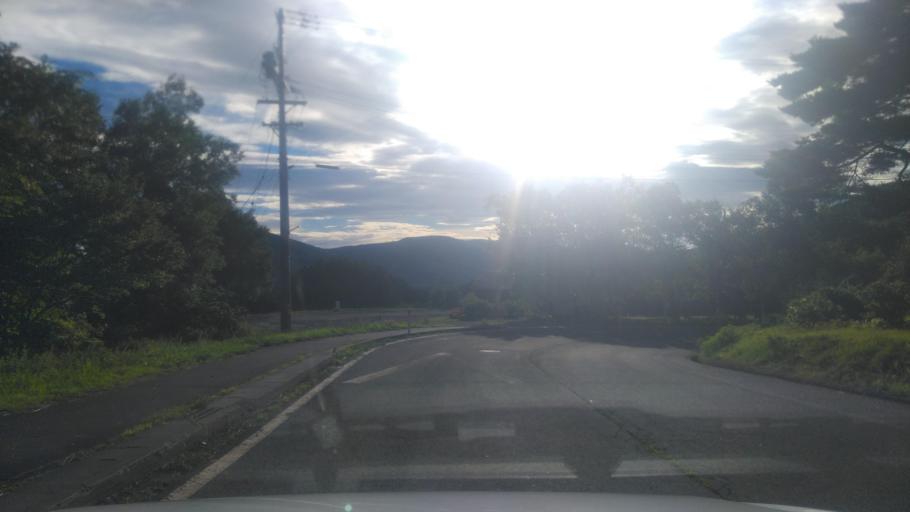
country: JP
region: Nagano
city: Suzaka
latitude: 36.5305
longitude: 138.3458
